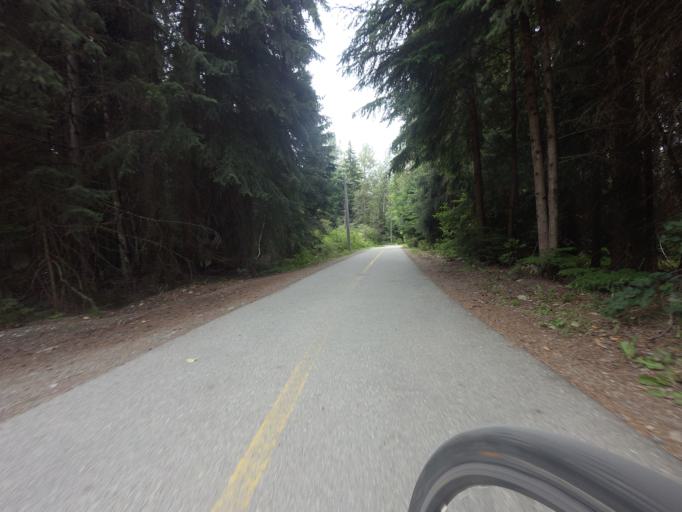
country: CA
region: British Columbia
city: Whistler
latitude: 50.1311
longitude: -122.9528
